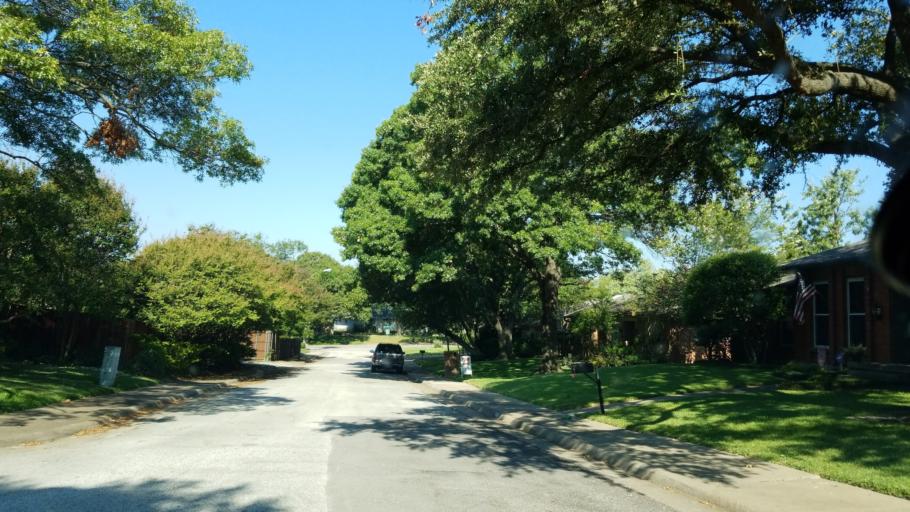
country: US
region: Texas
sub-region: Dallas County
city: Richardson
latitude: 32.9032
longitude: -96.7361
